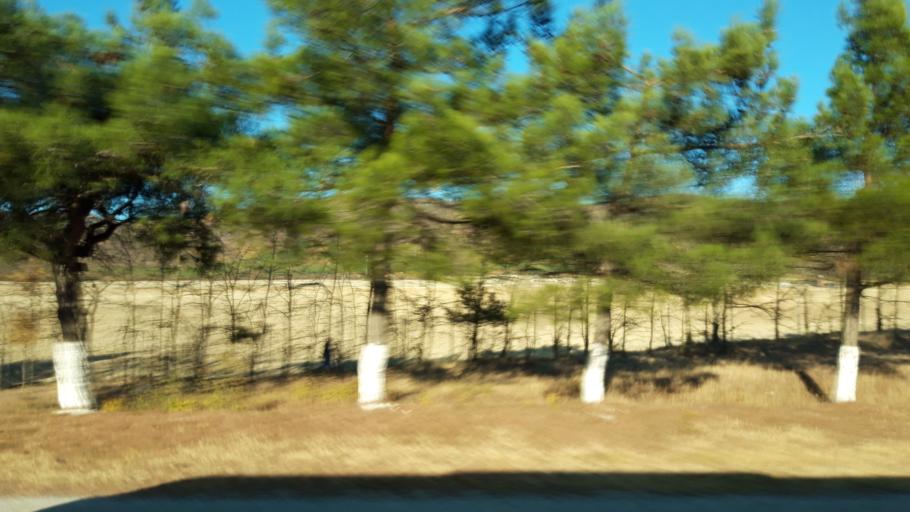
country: RU
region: Krasnodarskiy
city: Kabardinka
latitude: 44.6319
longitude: 38.0010
